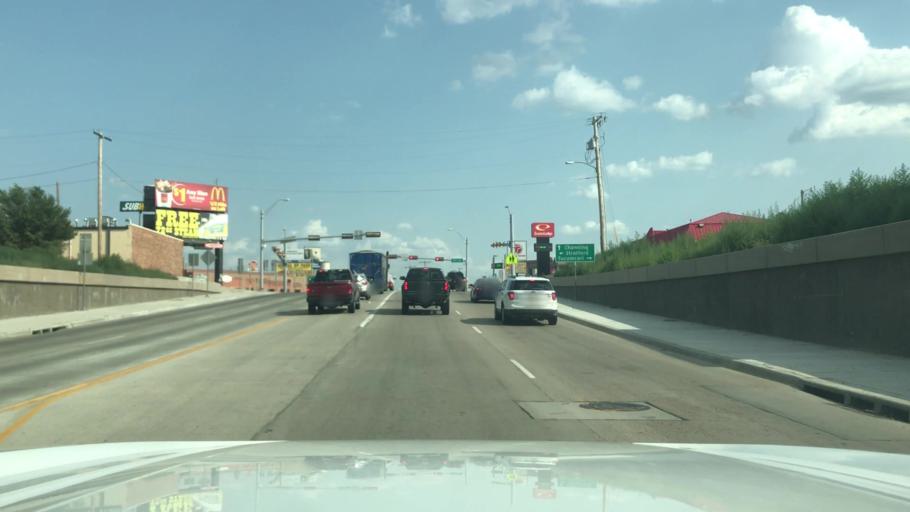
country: US
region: Texas
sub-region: Dallam County
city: Dalhart
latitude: 36.0660
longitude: -102.5217
